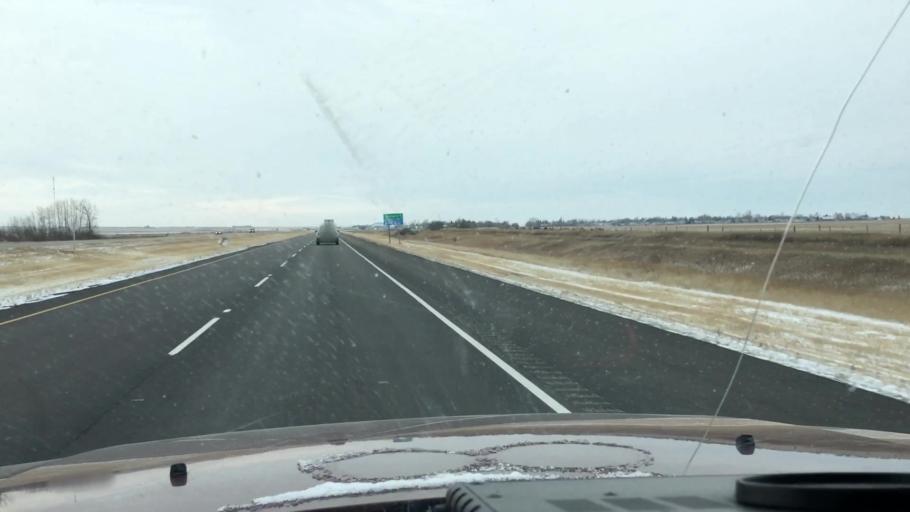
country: CA
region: Saskatchewan
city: Saskatoon
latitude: 51.8274
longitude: -106.5012
